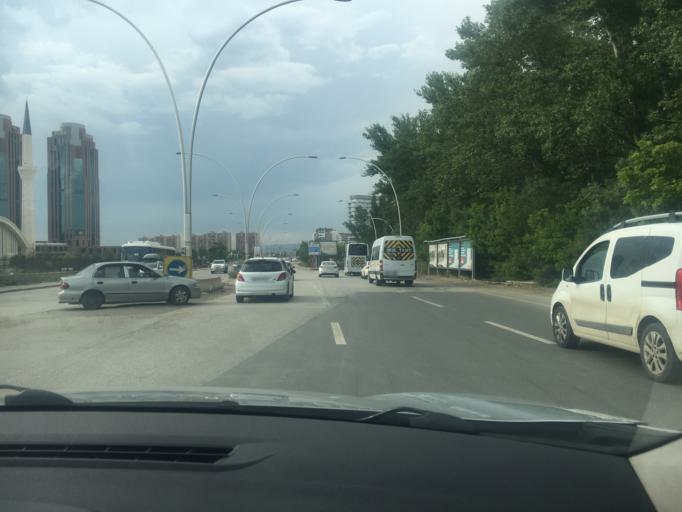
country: TR
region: Ankara
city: Batikent
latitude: 39.9050
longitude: 32.7651
